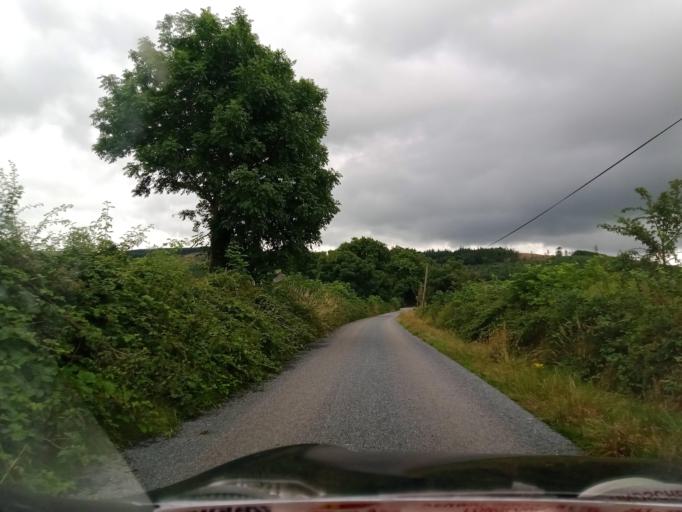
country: IE
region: Leinster
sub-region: Laois
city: Stradbally
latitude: 52.9600
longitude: -7.1852
